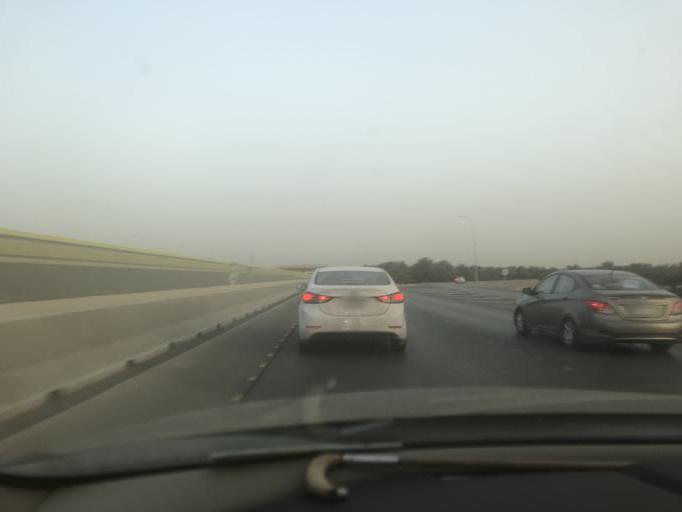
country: SA
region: Ar Riyad
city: Riyadh
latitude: 24.9265
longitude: 46.7189
